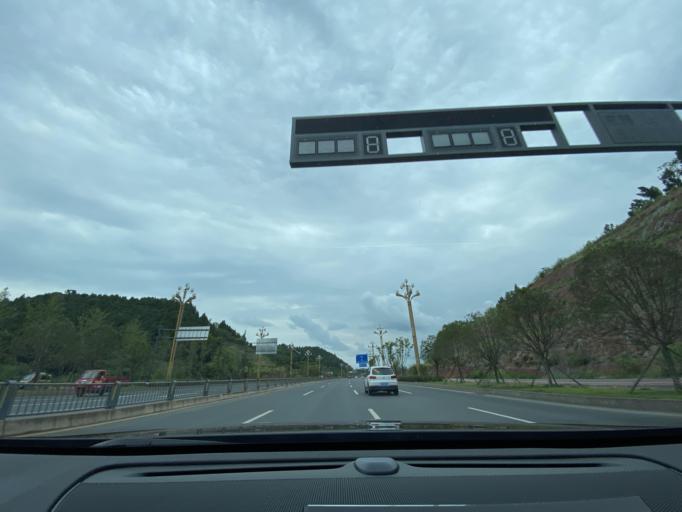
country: CN
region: Sichuan
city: Jiancheng
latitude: 30.4676
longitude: 104.4945
